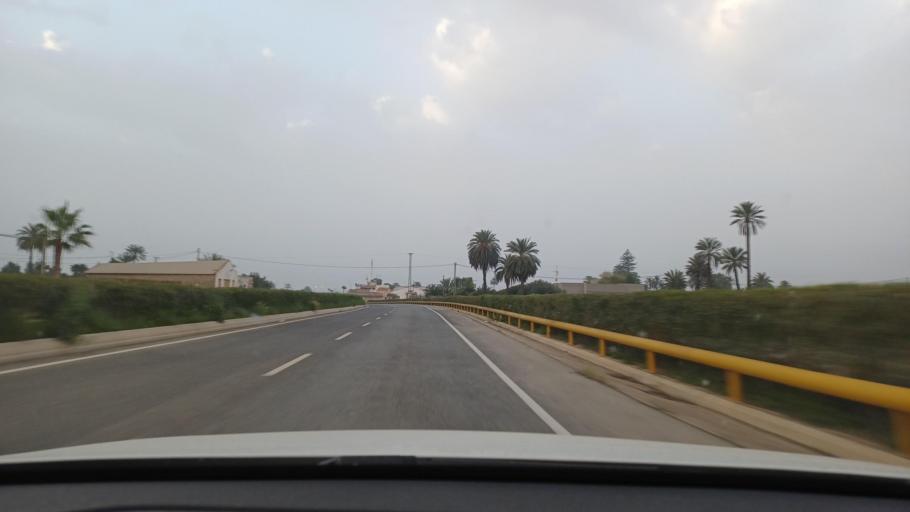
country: ES
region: Valencia
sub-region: Provincia de Alicante
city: Elche
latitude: 38.2268
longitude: -0.6992
